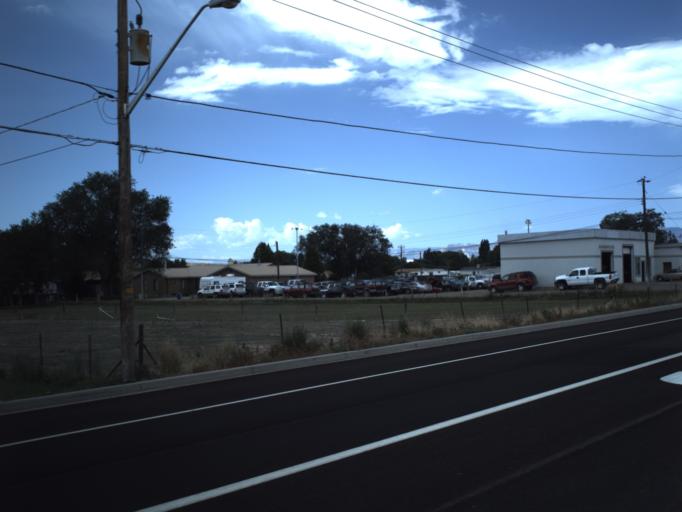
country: US
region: Utah
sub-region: Carbon County
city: Wellington
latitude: 39.5425
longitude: -110.7181
